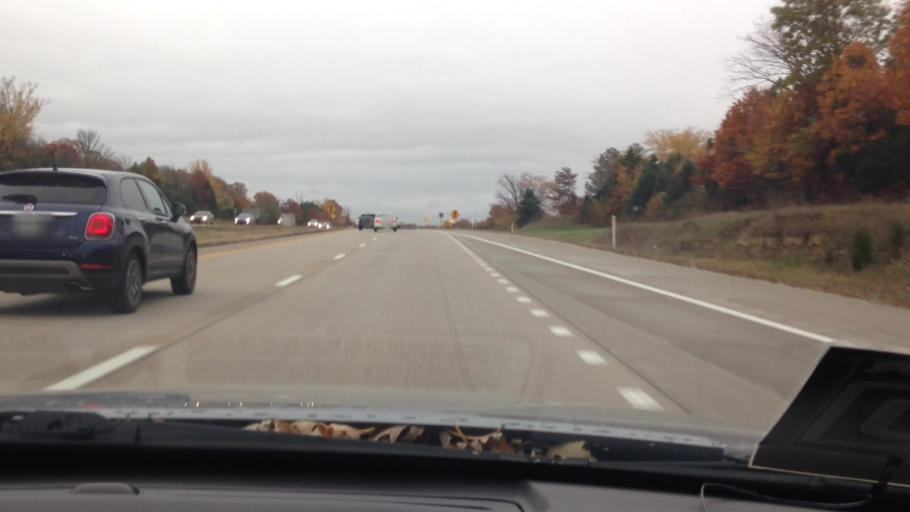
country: US
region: Kansas
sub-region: Wyandotte County
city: Bonner Springs
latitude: 39.1112
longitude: -94.8899
